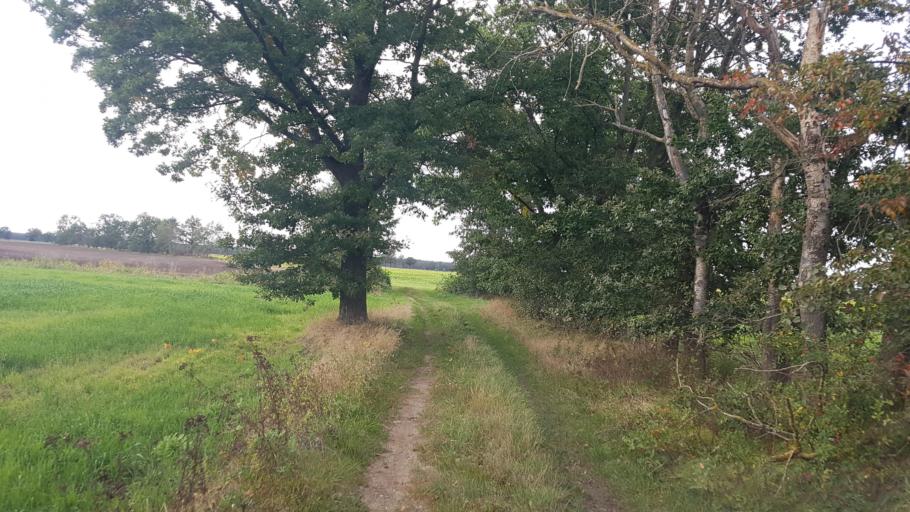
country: DE
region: Saxony
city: Nauwalde
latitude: 51.4676
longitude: 13.4337
